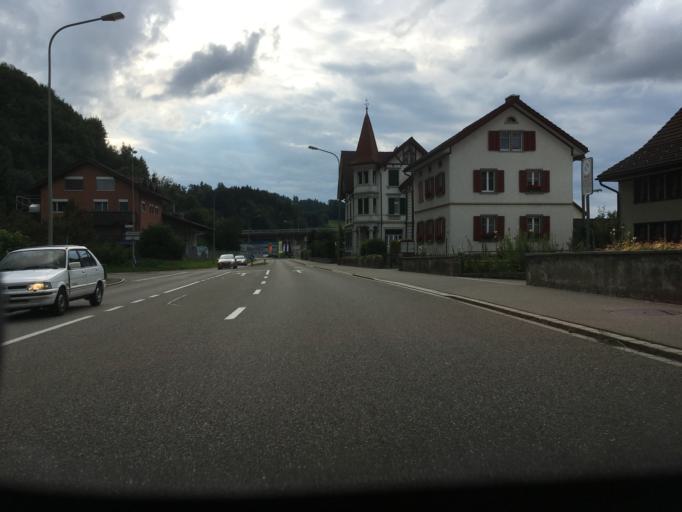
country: CH
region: Zurich
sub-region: Bezirk Pfaeffikon
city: Bauma
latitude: 47.3687
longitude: 8.8750
